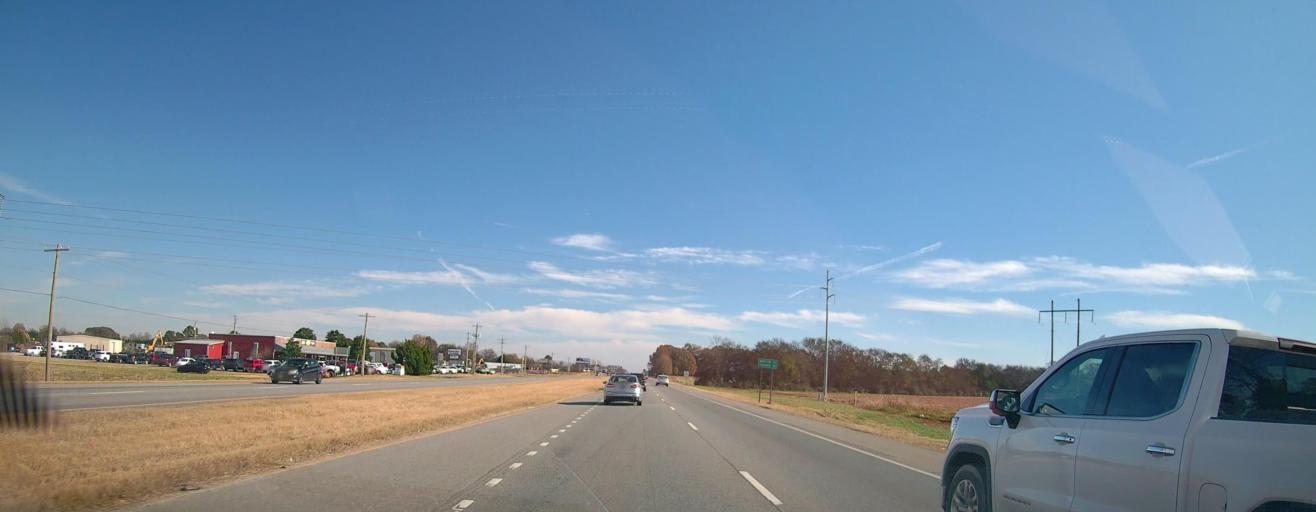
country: US
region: Alabama
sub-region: Colbert County
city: Muscle Shoals
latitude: 34.6967
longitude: -87.6321
